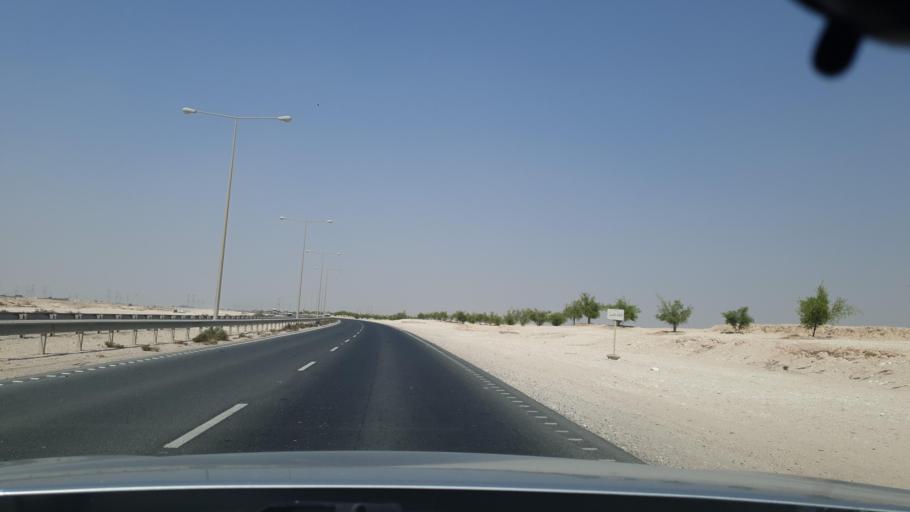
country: QA
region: Al Khawr
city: Al Khawr
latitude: 25.7346
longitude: 51.4927
